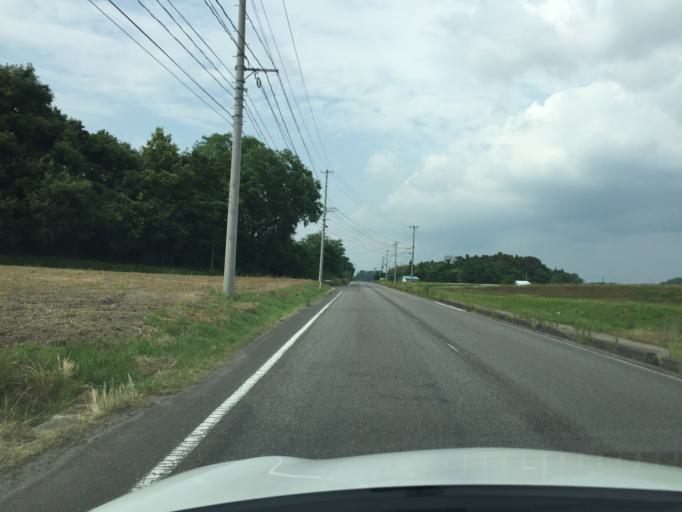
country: JP
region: Fukushima
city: Sukagawa
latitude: 37.2792
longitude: 140.4230
